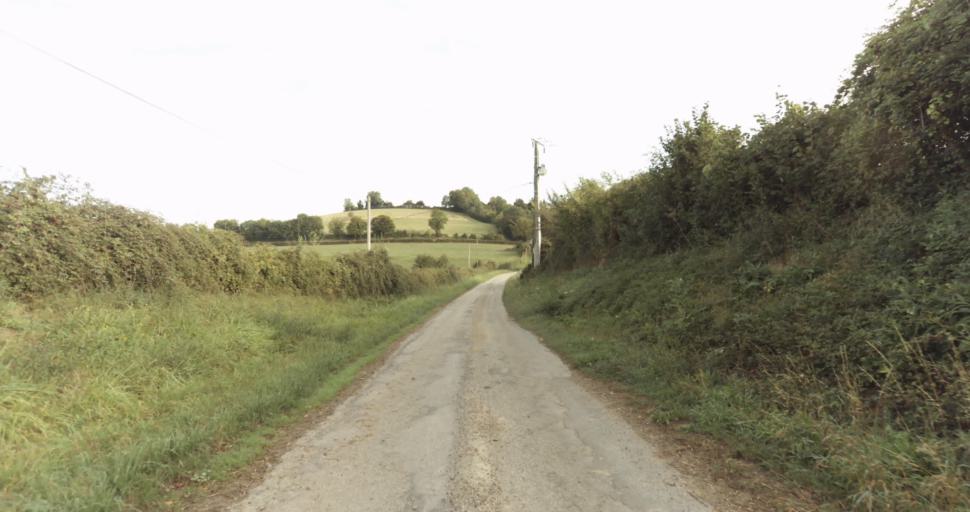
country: FR
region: Lower Normandy
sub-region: Departement de l'Orne
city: Vimoutiers
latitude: 48.8740
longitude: 0.2332
